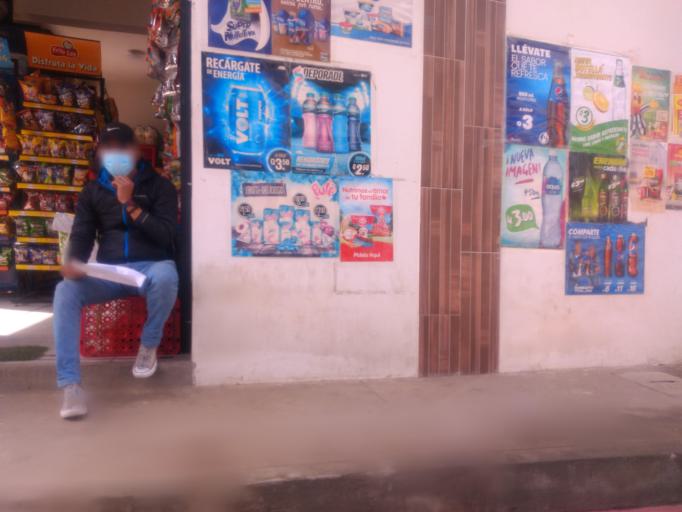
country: GT
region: Quetzaltenango
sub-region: Municipio de La Esperanza
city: La Esperanza
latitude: 14.8624
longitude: -91.5697
